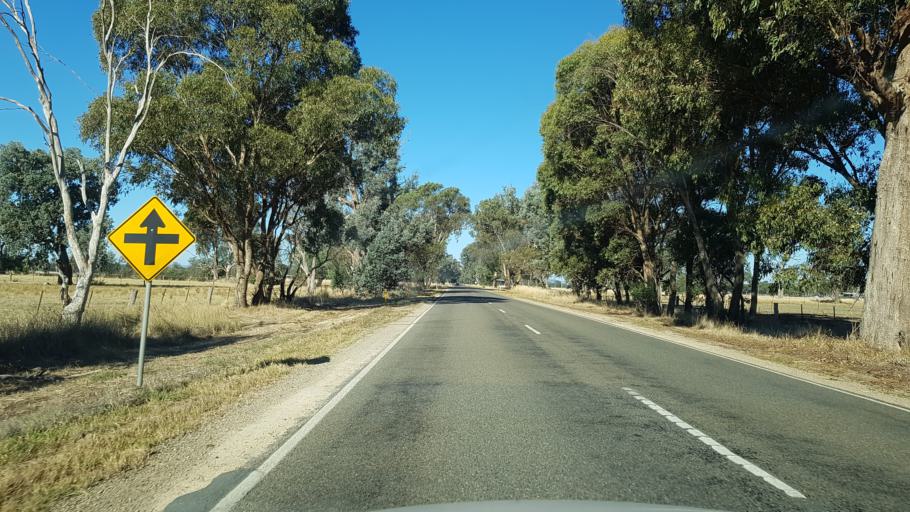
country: AU
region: Victoria
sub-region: Wangaratta
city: Wangaratta
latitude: -36.4355
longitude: 146.3216
